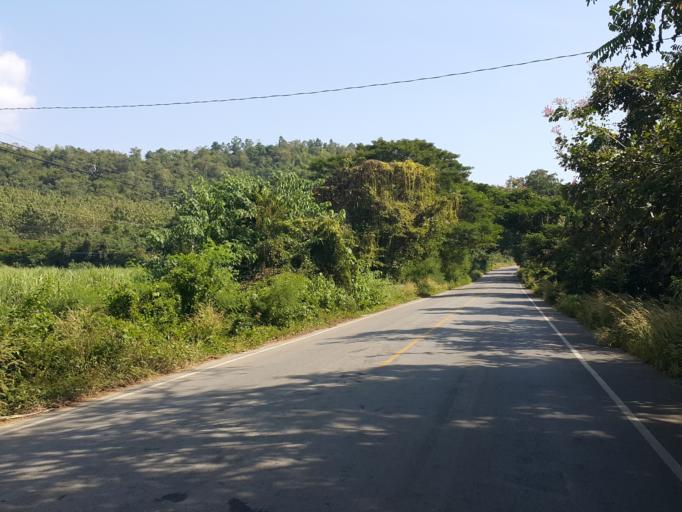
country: TH
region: Sukhothai
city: Thung Saliam
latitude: 17.3404
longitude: 99.4724
